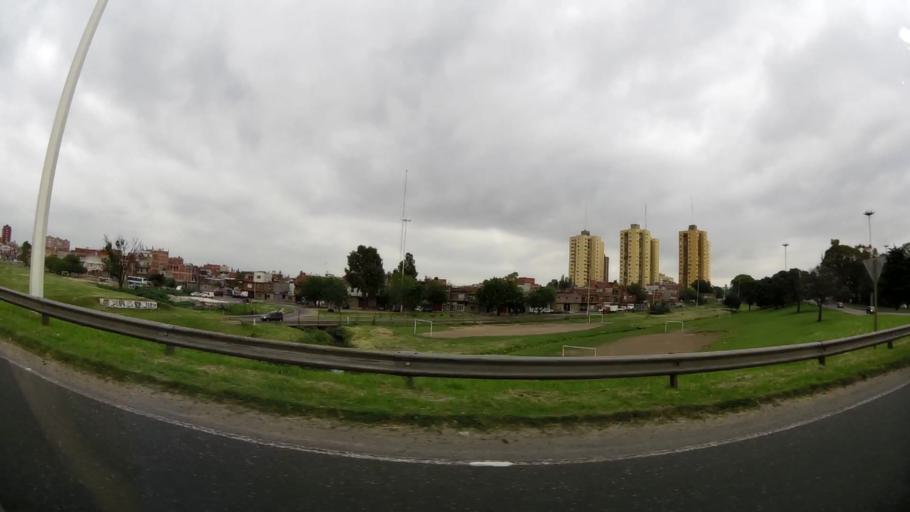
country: AR
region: Buenos Aires F.D.
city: Villa Lugano
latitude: -34.6877
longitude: -58.4861
